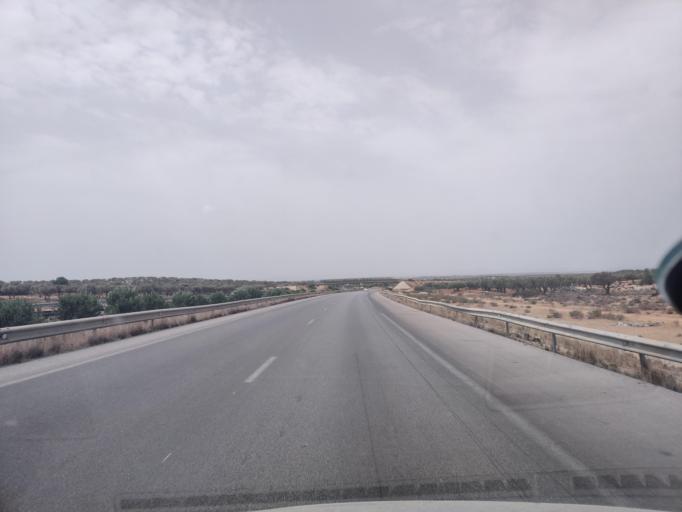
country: TN
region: Susah
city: Sidi Bou Ali
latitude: 35.9638
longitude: 10.4787
